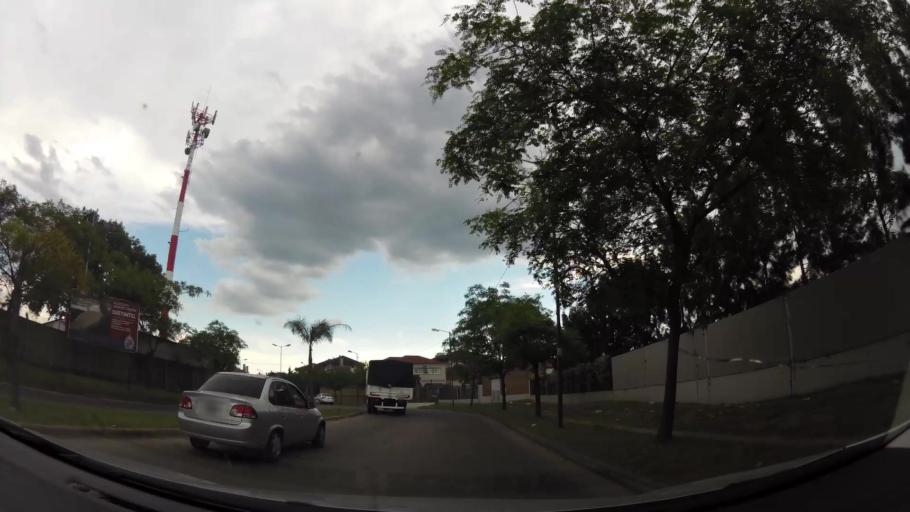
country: AR
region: Buenos Aires
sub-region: Partido de Tigre
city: Tigre
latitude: -34.4799
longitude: -58.5845
